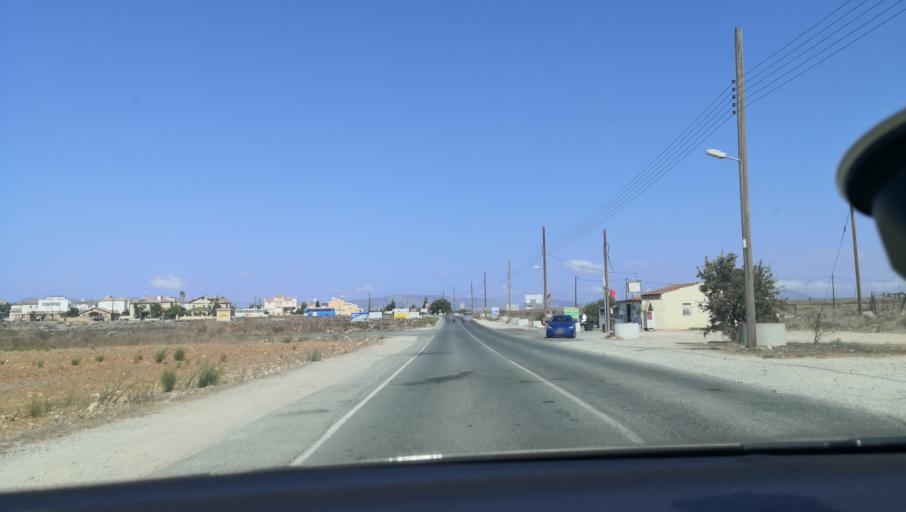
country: CY
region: Lefkosia
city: Kokkinotrimithia
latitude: 35.1638
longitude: 33.2020
